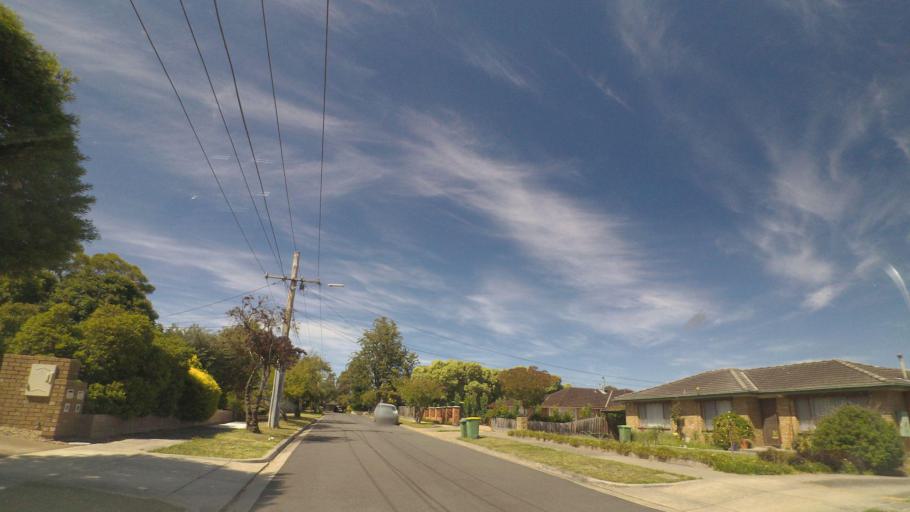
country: AU
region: Victoria
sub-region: Maroondah
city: Croydon North
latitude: -37.7716
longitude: 145.3044
